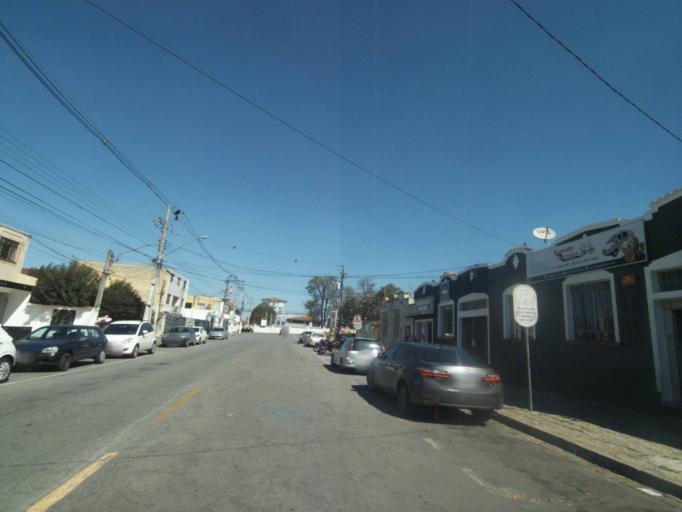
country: BR
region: Parana
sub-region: Curitiba
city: Curitiba
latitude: -25.3993
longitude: -49.2386
